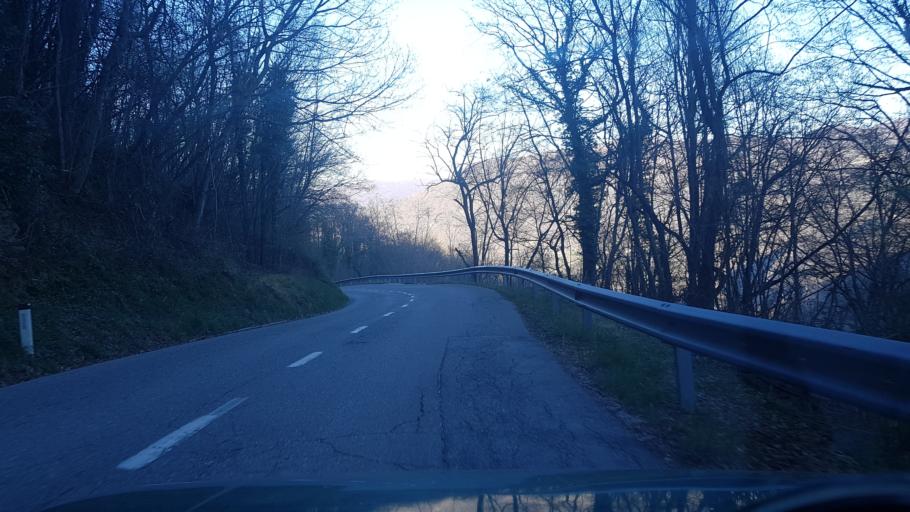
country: SI
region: Kanal
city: Deskle
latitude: 46.0286
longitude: 13.5787
